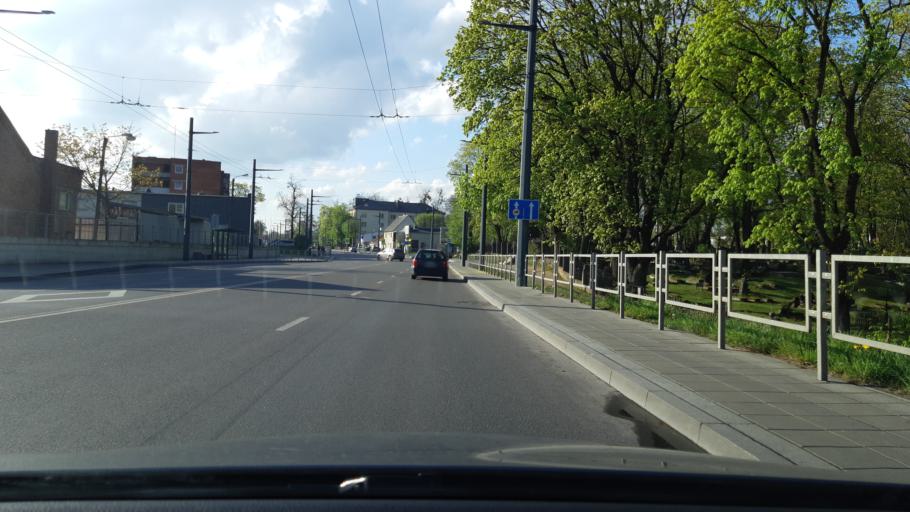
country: LT
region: Kauno apskritis
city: Dainava (Kaunas)
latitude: 54.8639
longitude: 23.9510
